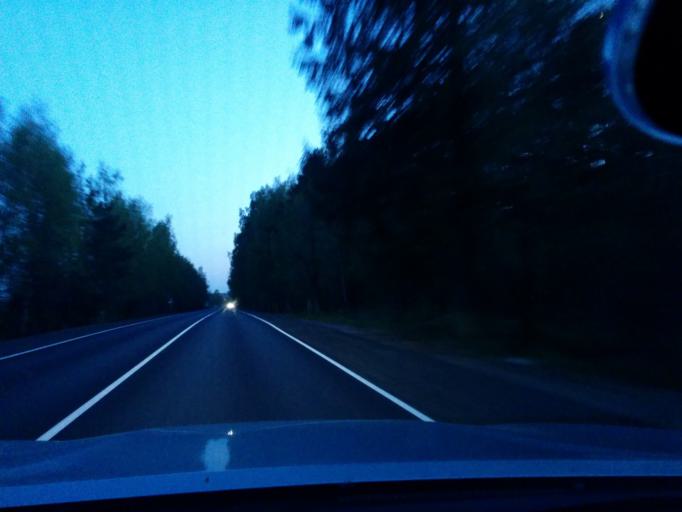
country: RU
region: Leningrad
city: Verkhniye Osel'ki
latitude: 60.1879
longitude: 30.4093
